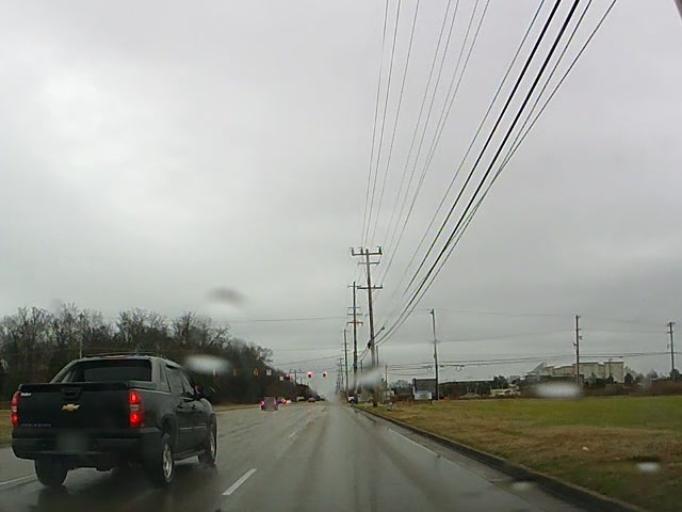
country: US
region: Tennessee
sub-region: Shelby County
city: Germantown
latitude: 35.0475
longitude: -89.7610
